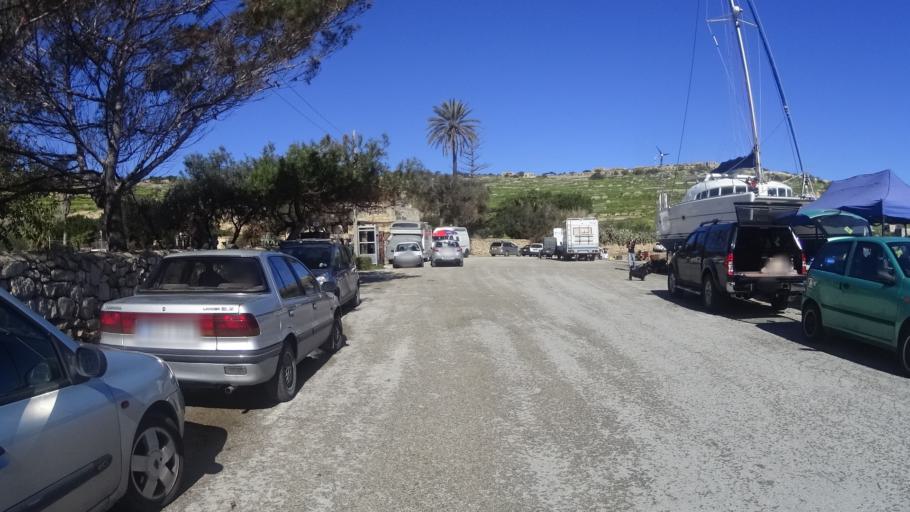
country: MT
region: Saint Paul's Bay
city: San Pawl il-Bahar
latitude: 35.9581
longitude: 14.3896
